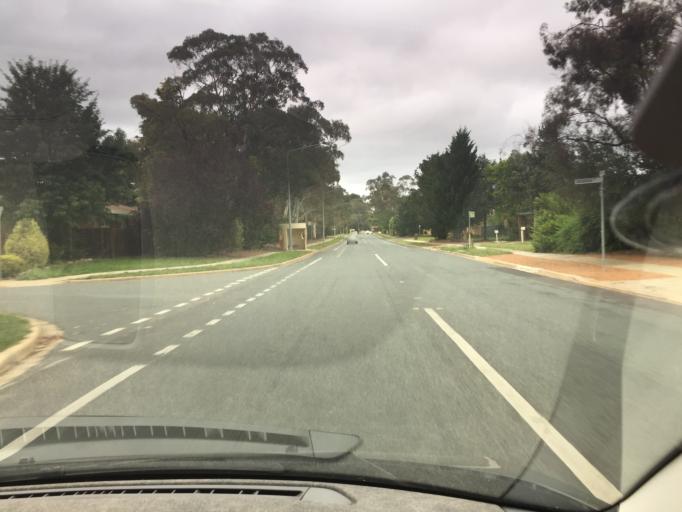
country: AU
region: Australian Capital Territory
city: Kaleen
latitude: -35.2264
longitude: 149.1112
